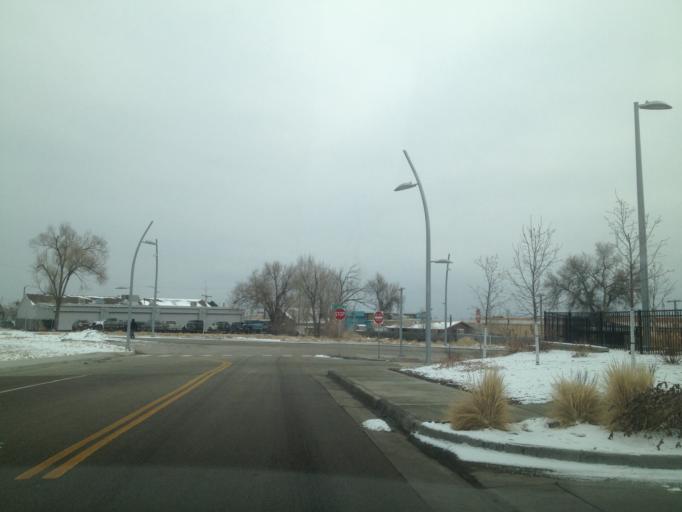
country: US
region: Colorado
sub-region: Adams County
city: Westminster
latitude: 39.8240
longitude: -105.0272
